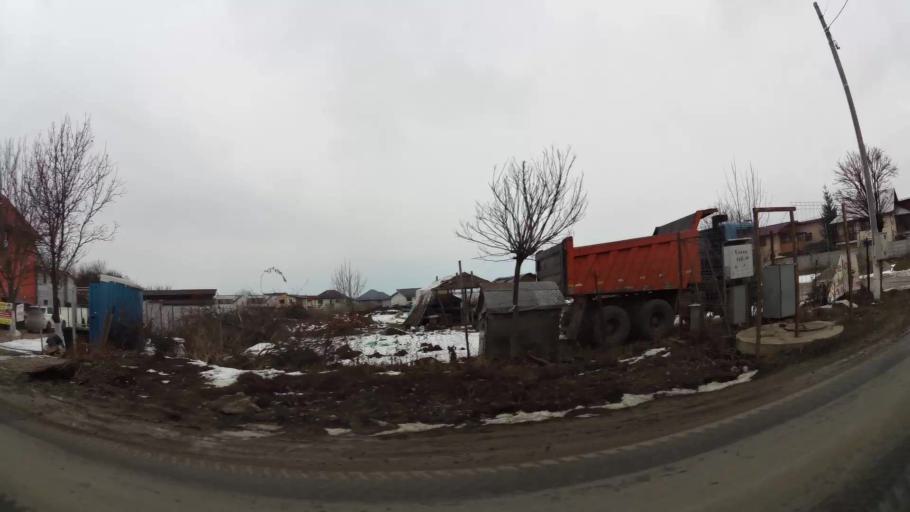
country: RO
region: Ilfov
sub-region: Comuna Tunari
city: Tunari
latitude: 44.5489
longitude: 26.1261
